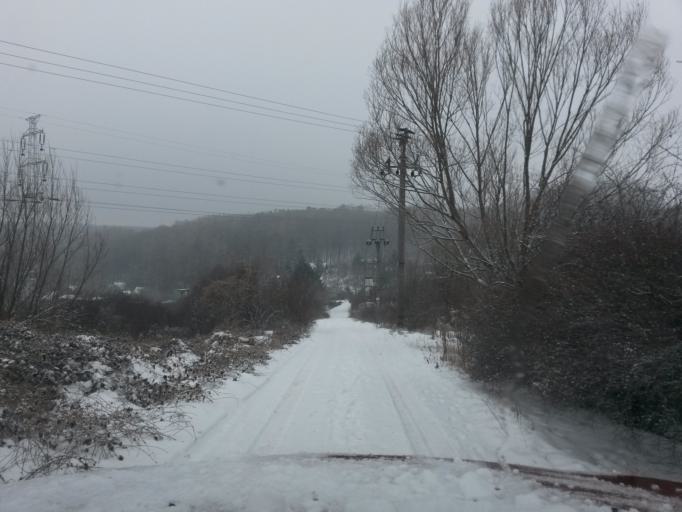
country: SK
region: Kosicky
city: Kosice
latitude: 48.7251
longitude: 21.3033
